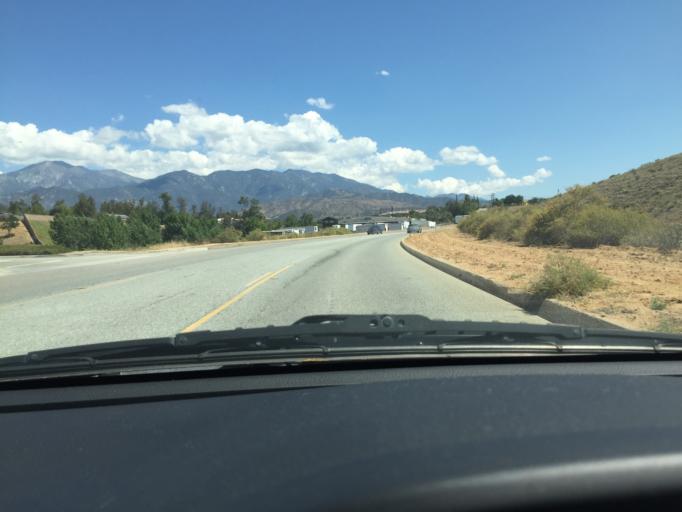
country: US
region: California
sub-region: Riverside County
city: Calimesa
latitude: 34.0155
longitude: -117.0731
